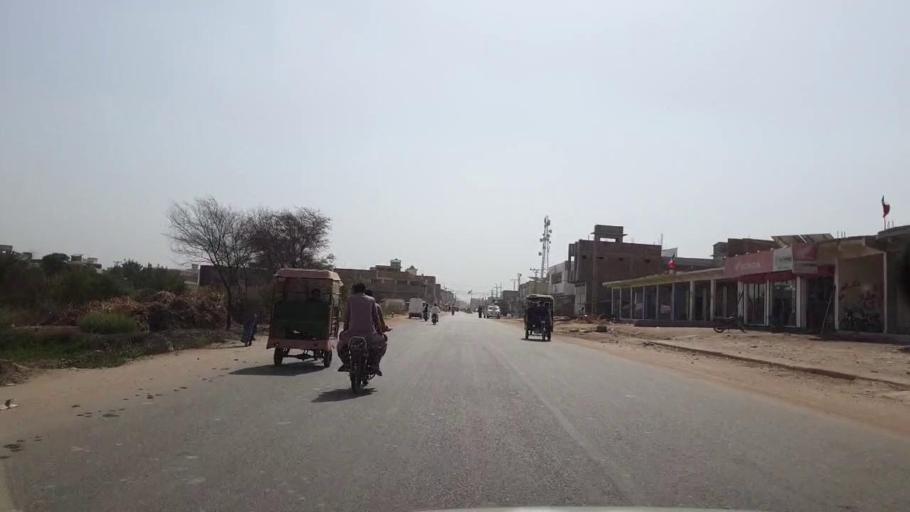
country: PK
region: Sindh
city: Matli
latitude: 25.0496
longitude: 68.6503
